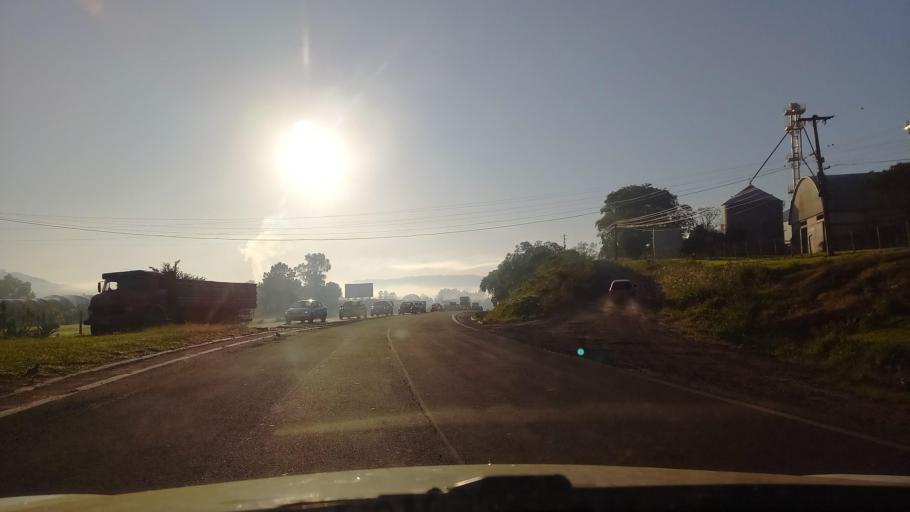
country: BR
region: Rio Grande do Sul
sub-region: Santa Cruz Do Sul
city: Santa Cruz do Sul
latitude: -29.6938
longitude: -52.4992
